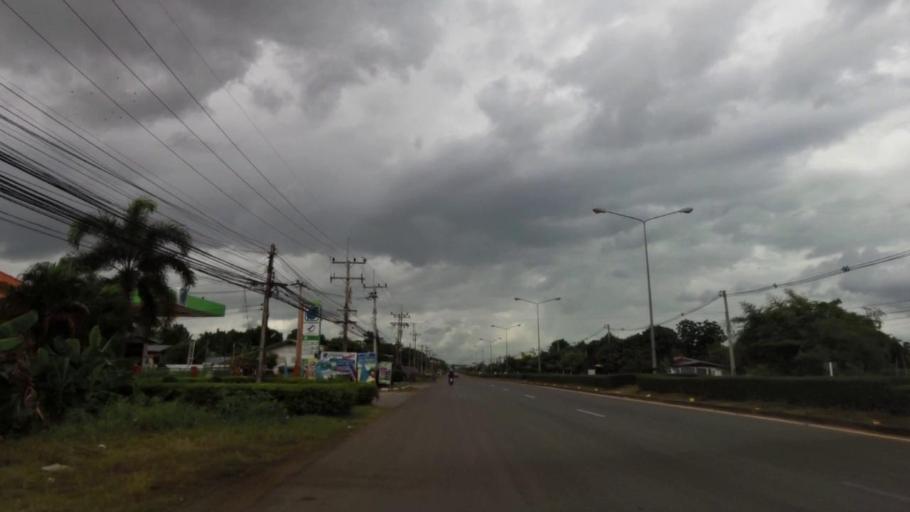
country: TH
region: Nakhon Sawan
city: Phai Sali
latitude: 15.5929
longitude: 100.6560
